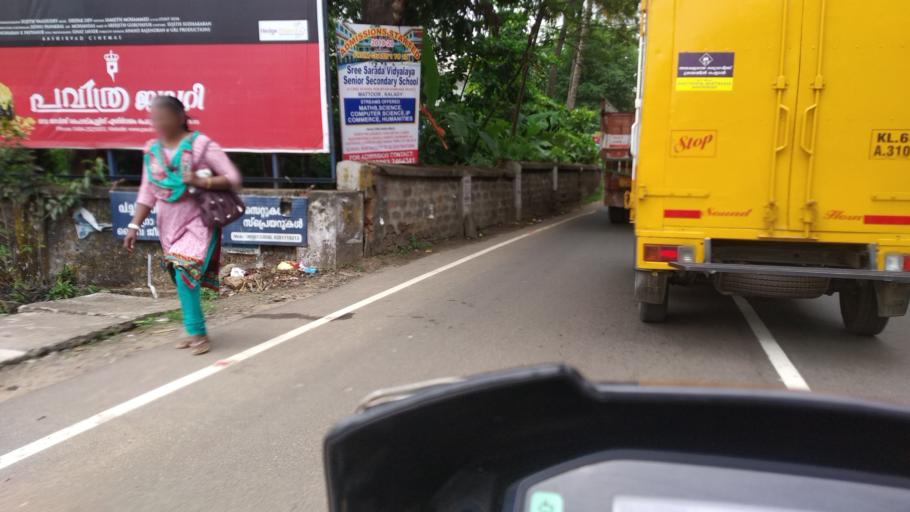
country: IN
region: Kerala
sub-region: Ernakulam
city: Perumpavur
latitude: 10.1180
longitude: 76.4770
